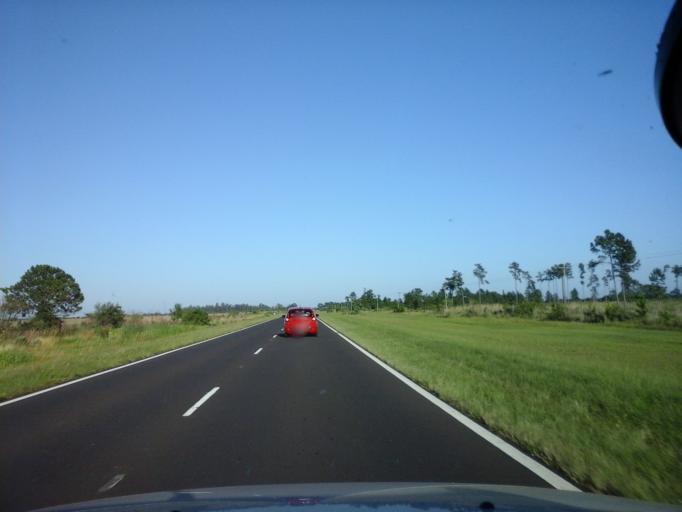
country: AR
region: Corrientes
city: Ita Ibate
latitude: -27.4945
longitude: -57.2668
